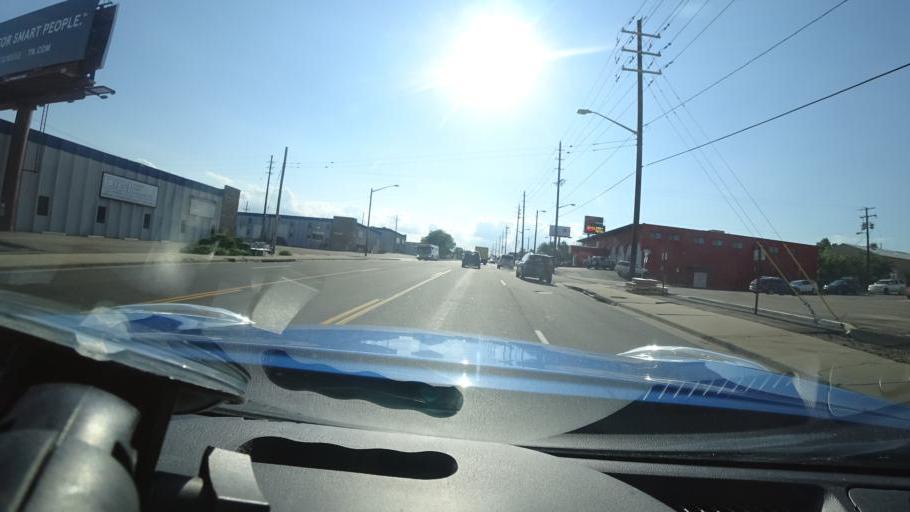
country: US
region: Colorado
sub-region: Arapahoe County
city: Englewood
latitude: 39.6786
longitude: -105.0060
